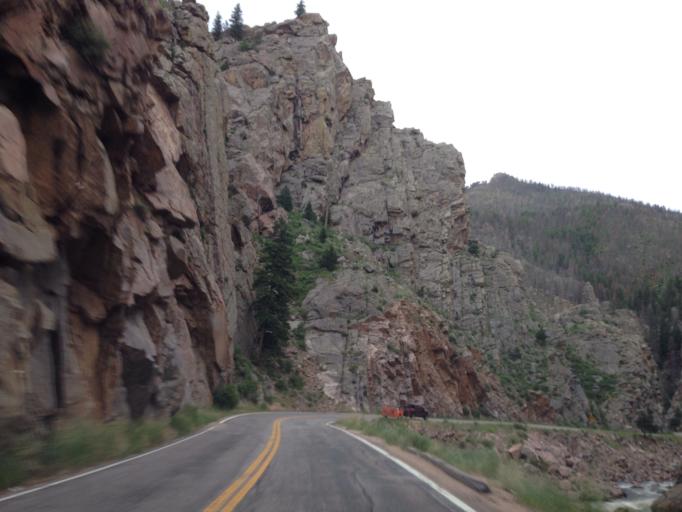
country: US
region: Colorado
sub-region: Larimer County
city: Laporte
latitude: 40.6775
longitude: -105.4304
